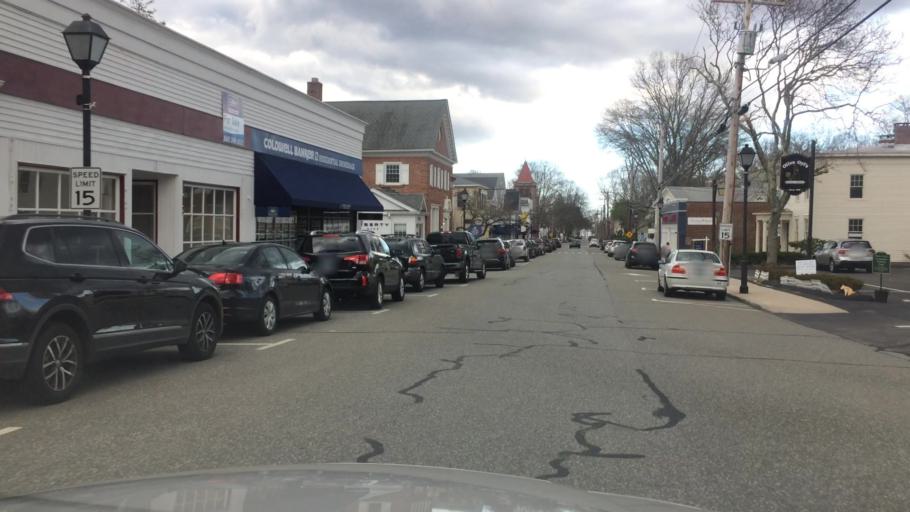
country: US
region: Connecticut
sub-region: Middlesex County
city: Essex Village
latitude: 41.3532
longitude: -72.3909
